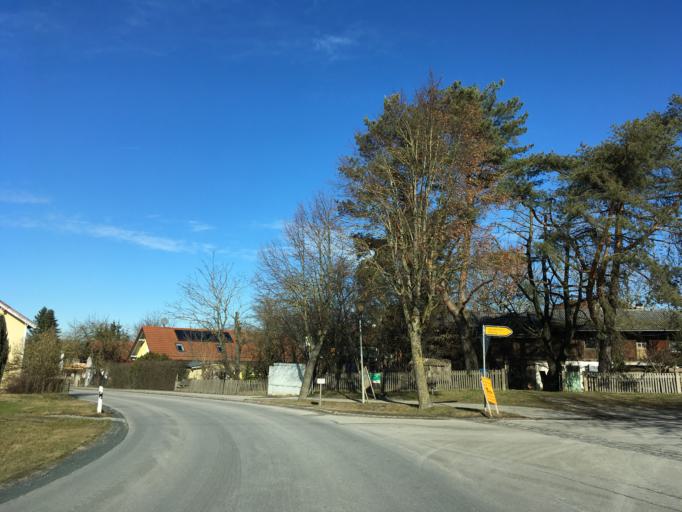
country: DE
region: Bavaria
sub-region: Upper Bavaria
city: Obertaufkirchen
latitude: 48.2580
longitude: 12.2852
